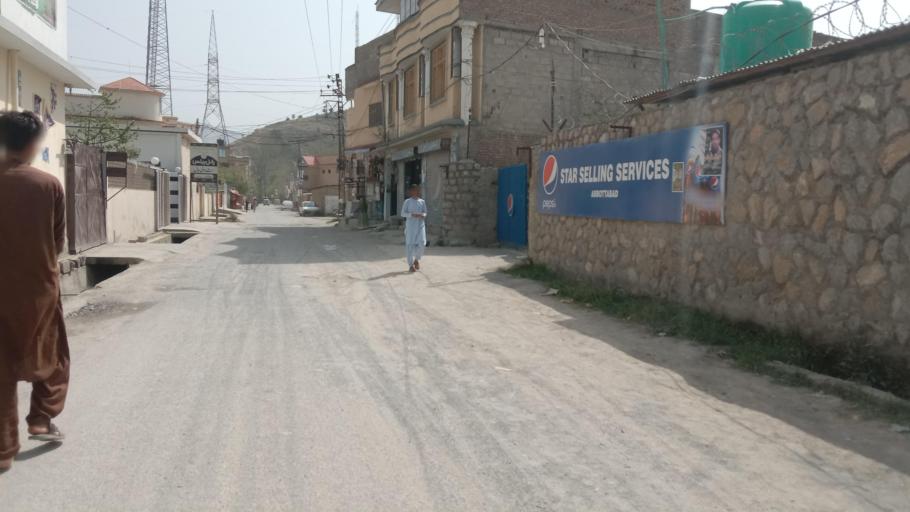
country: PK
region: Khyber Pakhtunkhwa
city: Abbottabad
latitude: 34.1566
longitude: 73.2595
